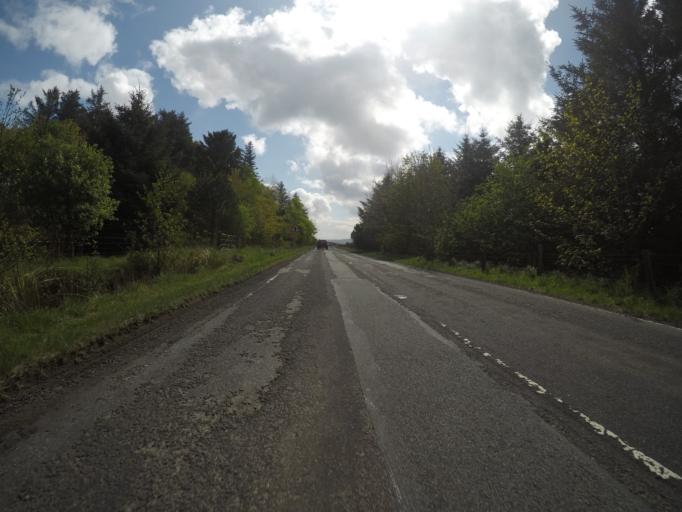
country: GB
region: Scotland
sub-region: Highland
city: Portree
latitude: 57.5694
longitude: -6.3645
